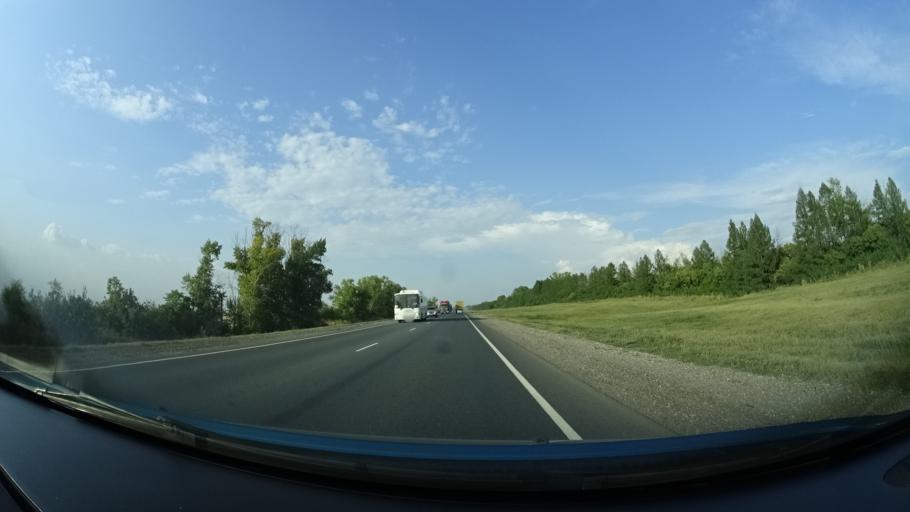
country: RU
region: Samara
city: Krasnyy Yar
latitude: 53.6439
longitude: 50.7339
